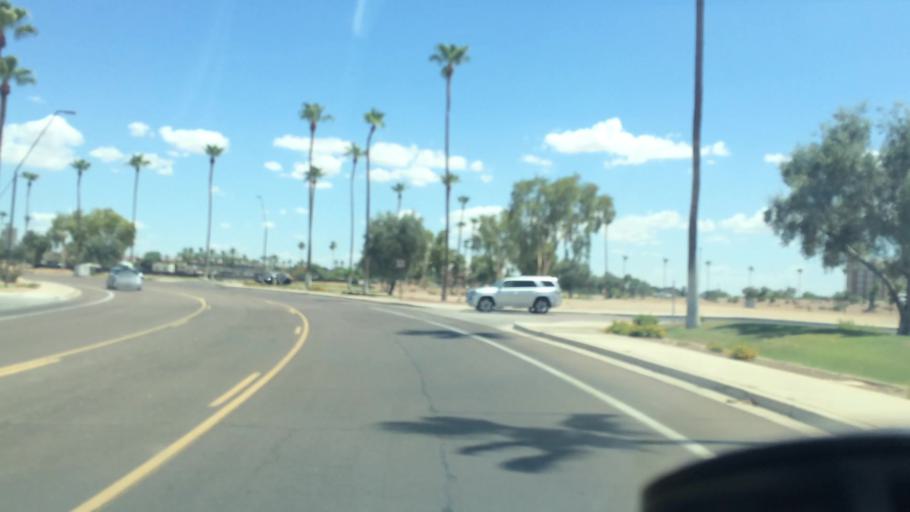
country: US
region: Arizona
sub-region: Maricopa County
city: Guadalupe
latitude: 33.3377
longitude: -111.9694
